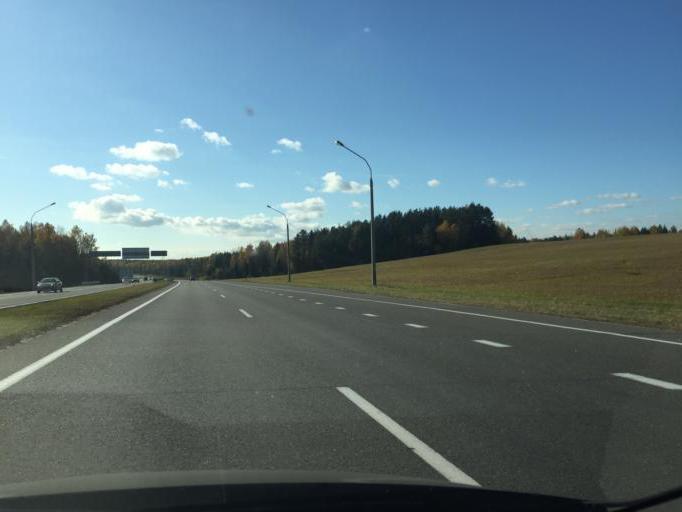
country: BY
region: Minsk
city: Slabada
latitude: 53.9451
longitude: 27.9713
